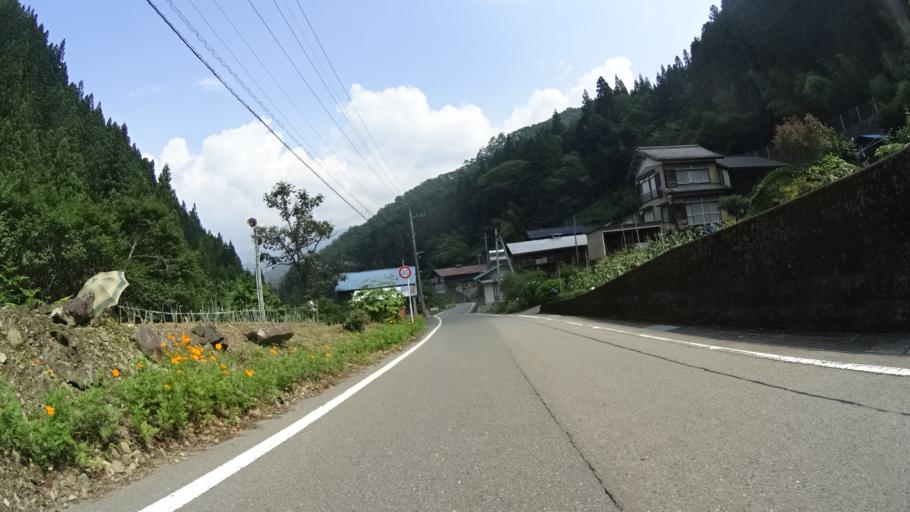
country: JP
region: Gunma
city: Tomioka
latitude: 36.0693
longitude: 138.8310
